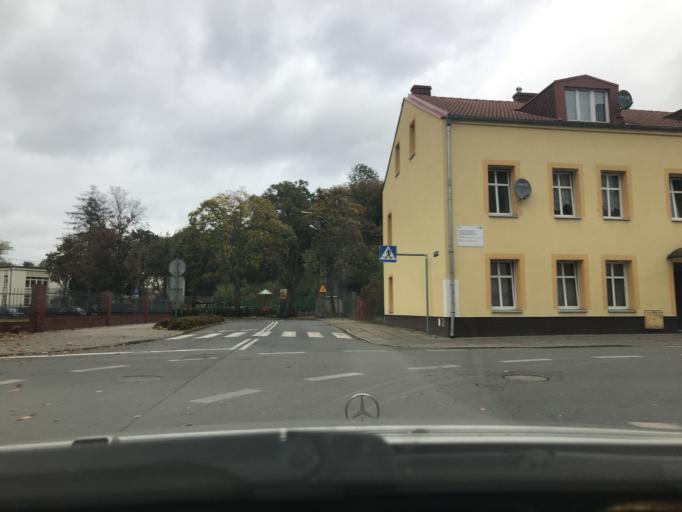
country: PL
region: West Pomeranian Voivodeship
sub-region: Swinoujscie
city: Swinoujscie
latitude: 53.9104
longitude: 14.2470
